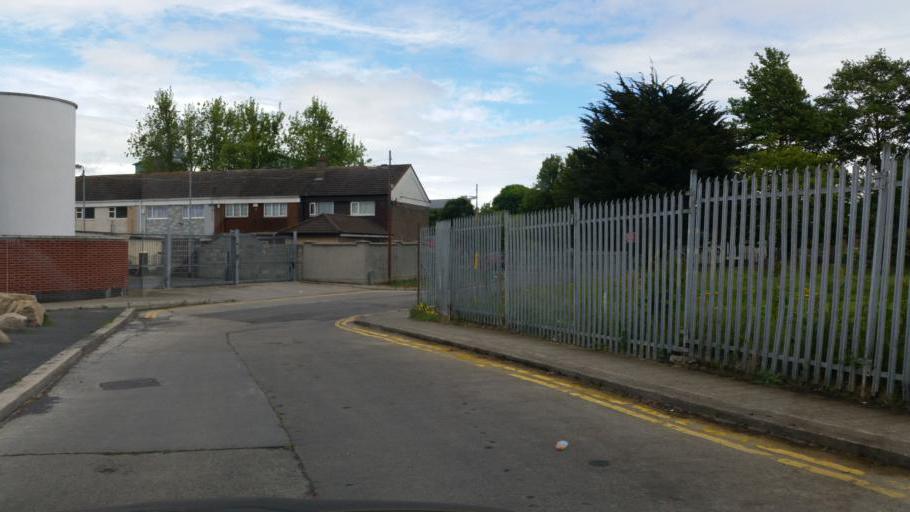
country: IE
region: Leinster
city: Ballymun
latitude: 53.3924
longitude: -6.2664
